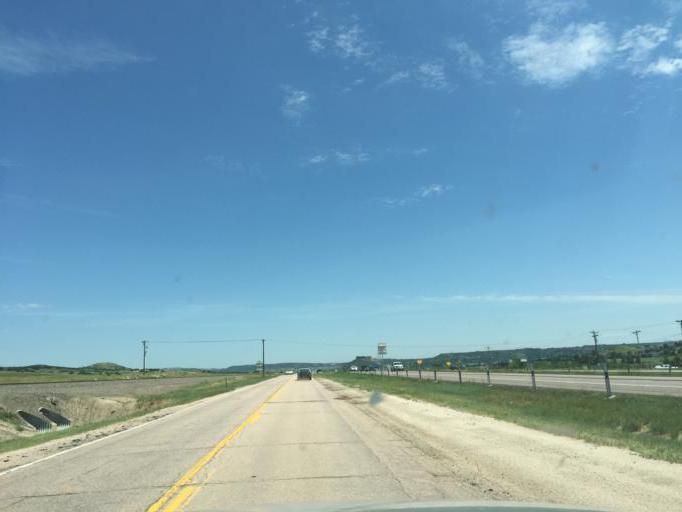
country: US
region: Colorado
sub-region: Douglas County
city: Castle Rock
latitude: 39.3390
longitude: -104.8763
